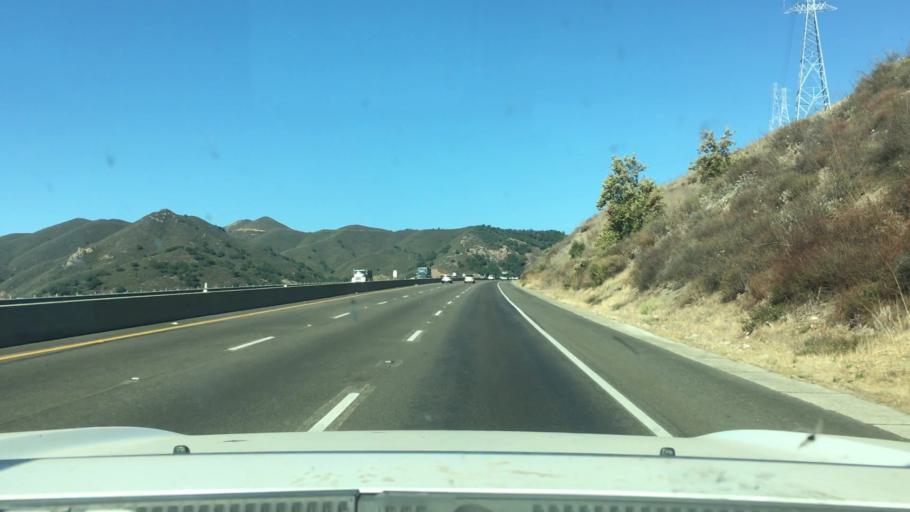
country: US
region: California
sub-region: San Luis Obispo County
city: San Luis Obispo
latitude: 35.3304
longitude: -120.6219
